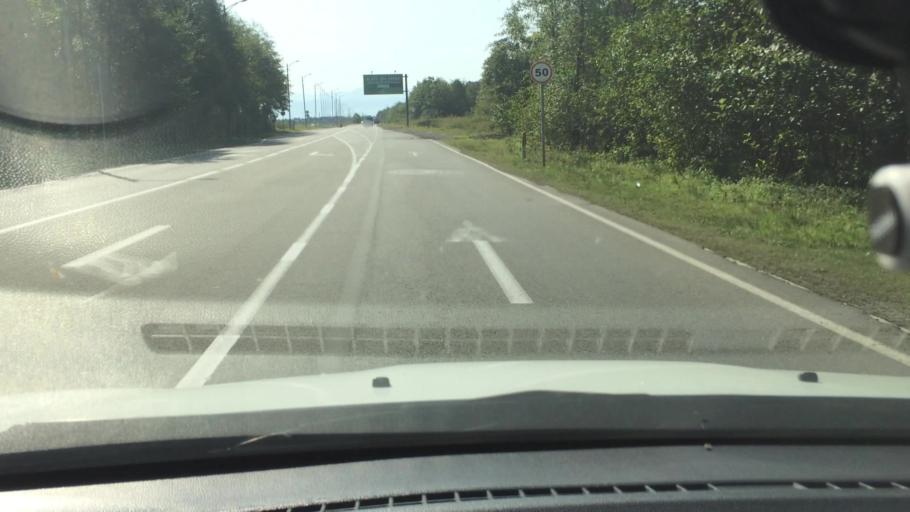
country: GE
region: Guria
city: Urek'i
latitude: 41.9427
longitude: 41.7708
